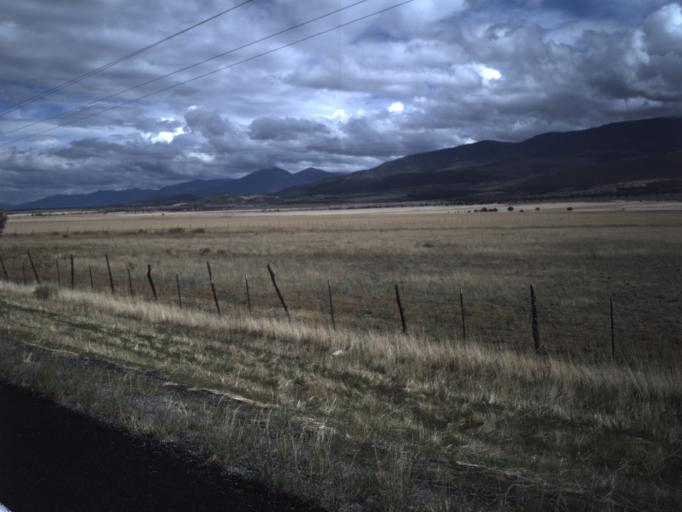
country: US
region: Utah
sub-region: Millard County
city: Fillmore
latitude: 38.8385
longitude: -112.4270
